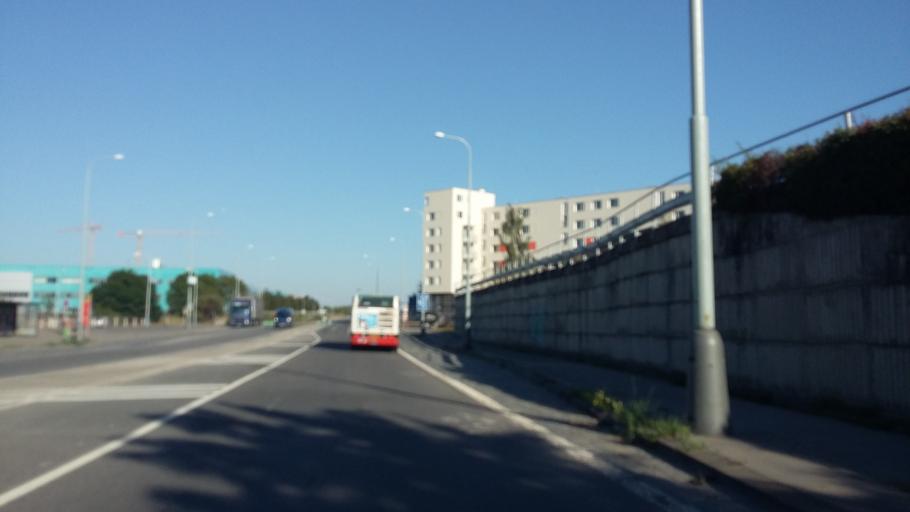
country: CZ
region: Praha
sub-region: Praha 18
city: Letnany
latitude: 50.1418
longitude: 14.5144
